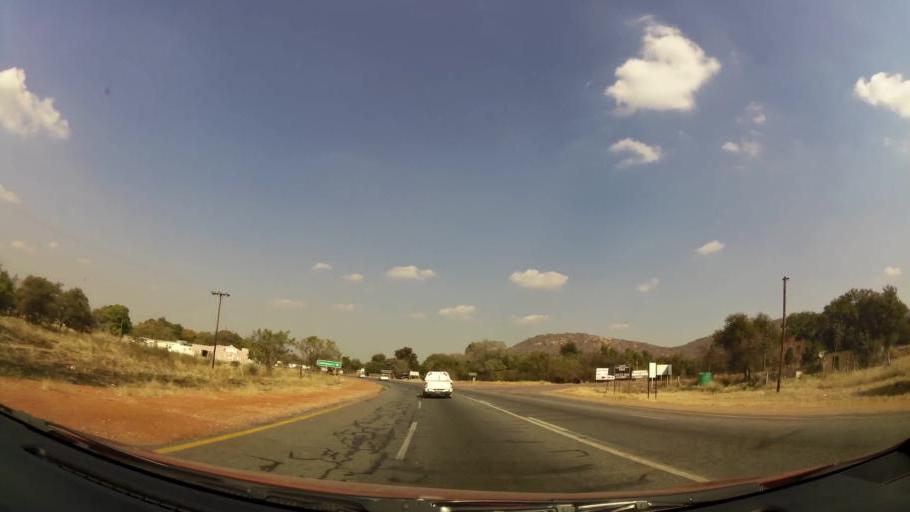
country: ZA
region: North-West
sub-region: Bojanala Platinum District Municipality
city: Rustenburg
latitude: -25.4919
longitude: 27.0858
